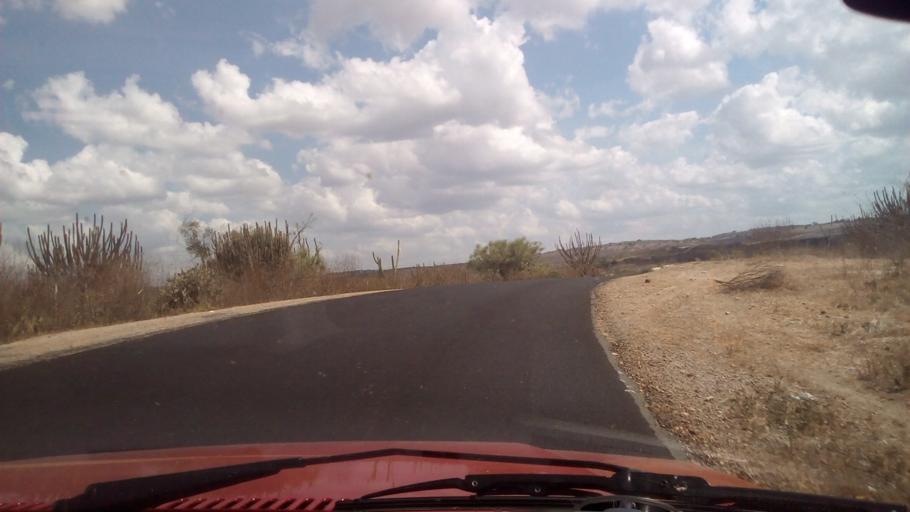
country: BR
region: Paraiba
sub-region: Bananeiras
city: Bananeiras
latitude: -6.7209
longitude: -35.7131
